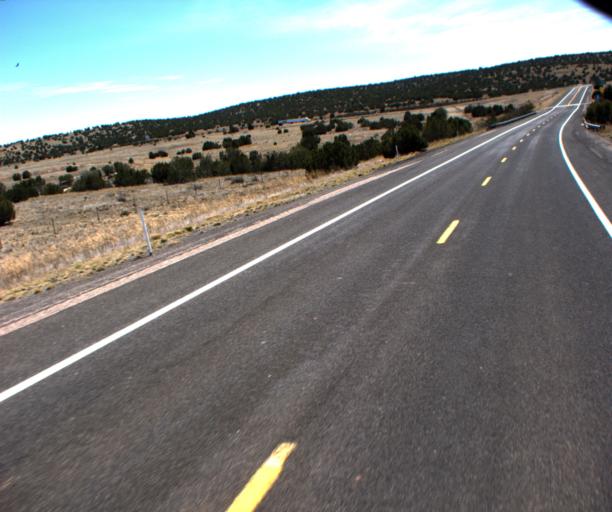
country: US
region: Arizona
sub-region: Mohave County
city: Peach Springs
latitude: 35.3248
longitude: -112.8911
